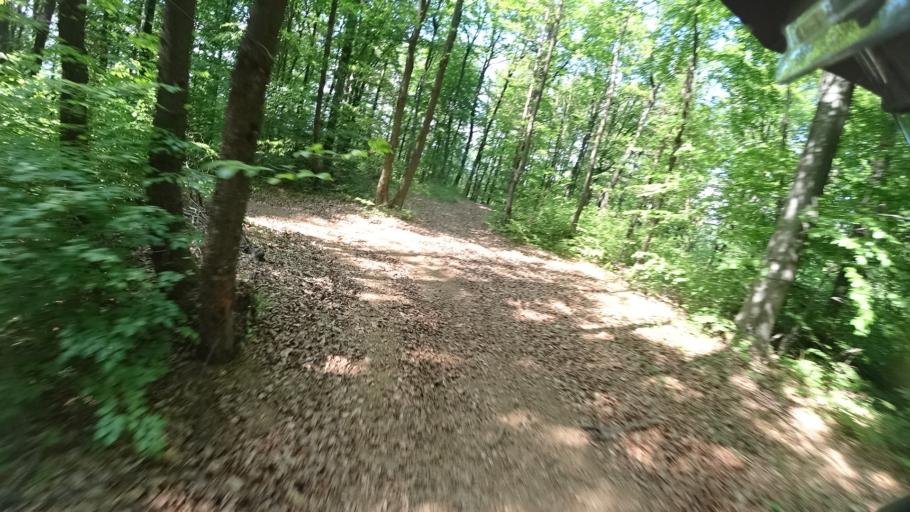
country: HR
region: Grad Zagreb
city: Kasina
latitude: 45.9449
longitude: 15.9615
